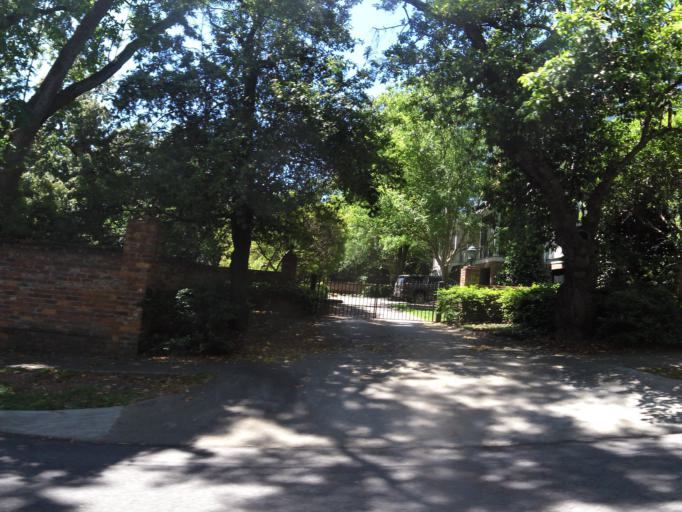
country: US
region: Georgia
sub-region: Richmond County
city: Augusta
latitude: 33.4764
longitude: -82.0126
